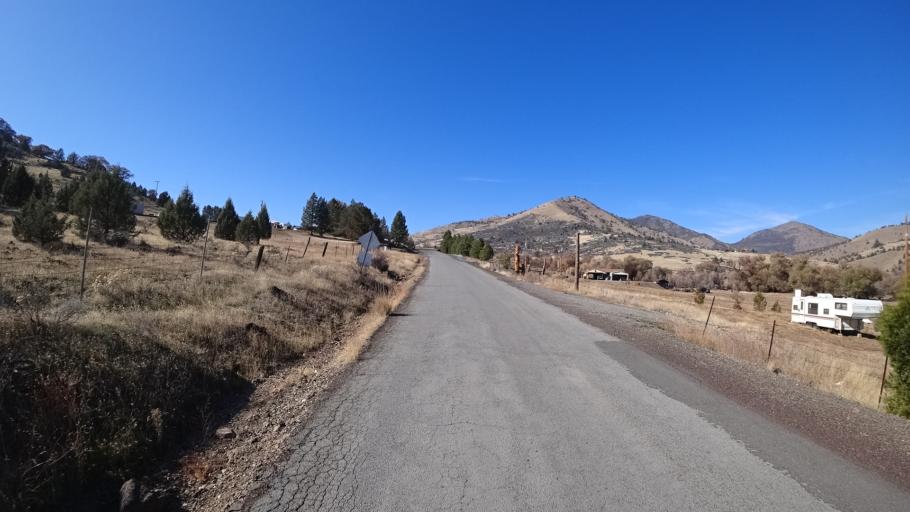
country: US
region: California
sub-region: Siskiyou County
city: Yreka
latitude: 41.7730
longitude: -122.5949
